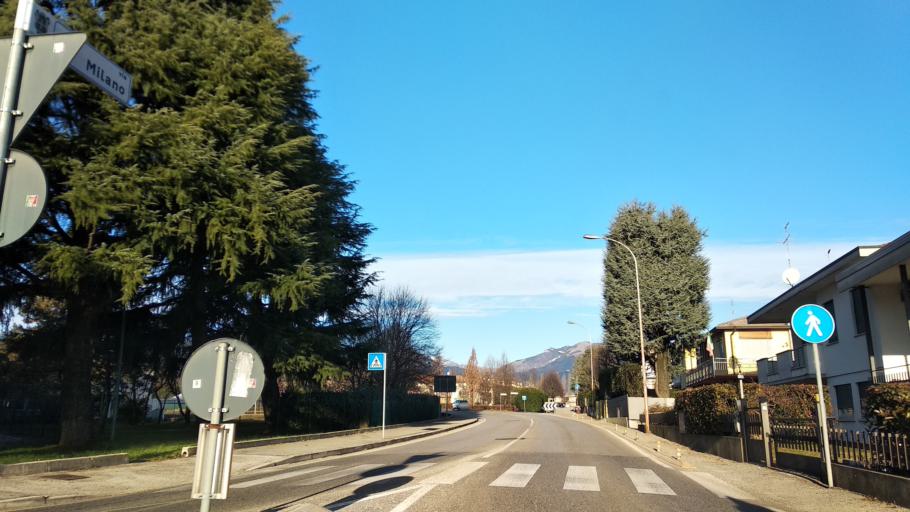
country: IT
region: Veneto
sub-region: Provincia di Vicenza
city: Malo
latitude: 45.6622
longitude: 11.4091
